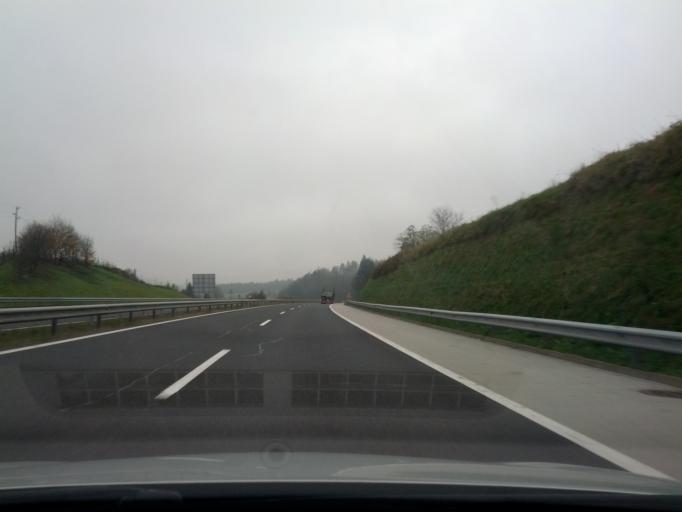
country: SI
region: Ivancna Gorica
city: Ivancna Gorica
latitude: 45.9346
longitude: 14.8147
